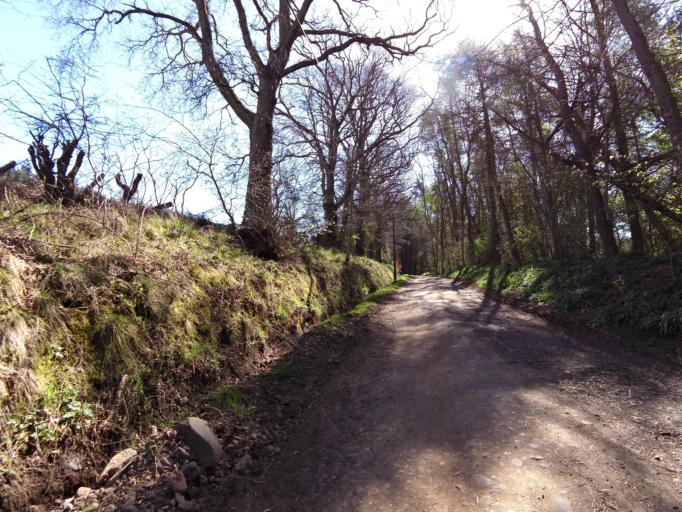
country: GB
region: Scotland
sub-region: Fife
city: Cupar
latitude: 56.3929
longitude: -3.0722
